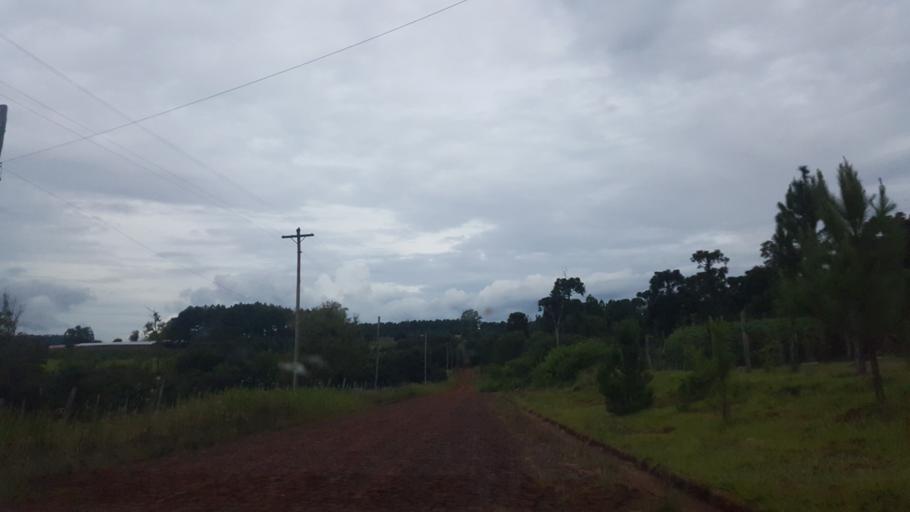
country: AR
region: Misiones
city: Capiovi
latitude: -26.9257
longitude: -55.0503
